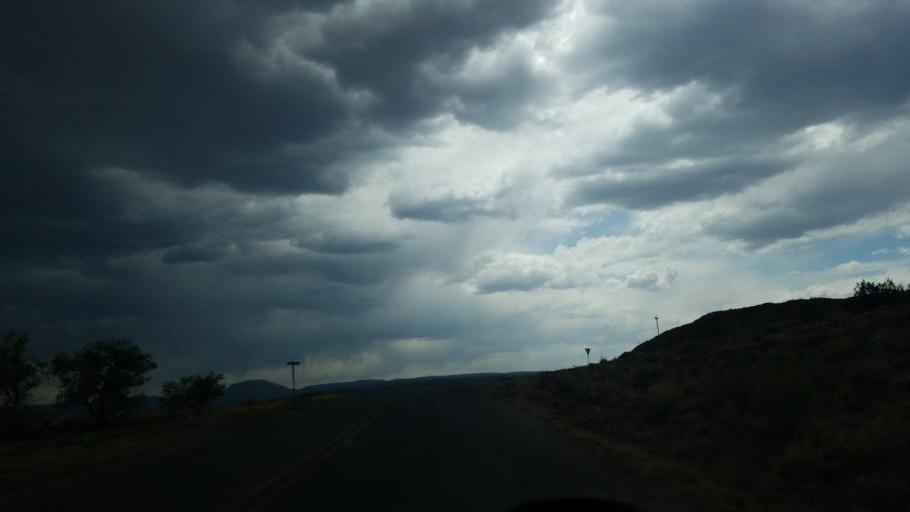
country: US
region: New Mexico
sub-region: Cibola County
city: Grants
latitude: 35.1593
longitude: -107.8504
